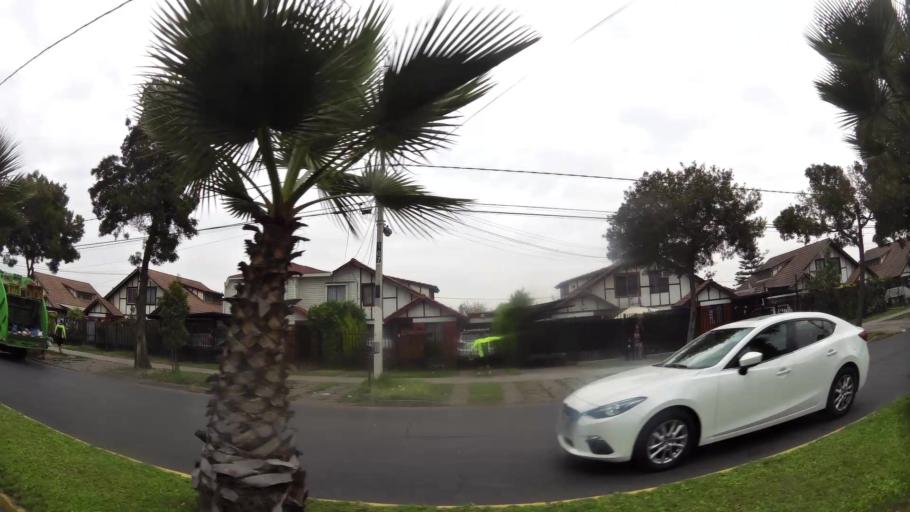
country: CL
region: Santiago Metropolitan
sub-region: Provincia de Santiago
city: Villa Presidente Frei, Nunoa, Santiago, Chile
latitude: -33.4980
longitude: -70.6022
